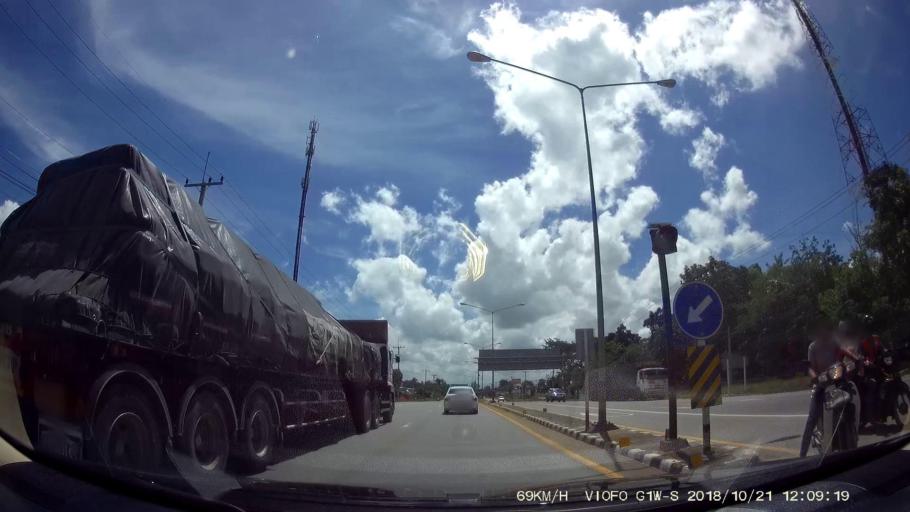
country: TH
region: Chaiyaphum
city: Chatturat
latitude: 15.4224
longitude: 101.8323
